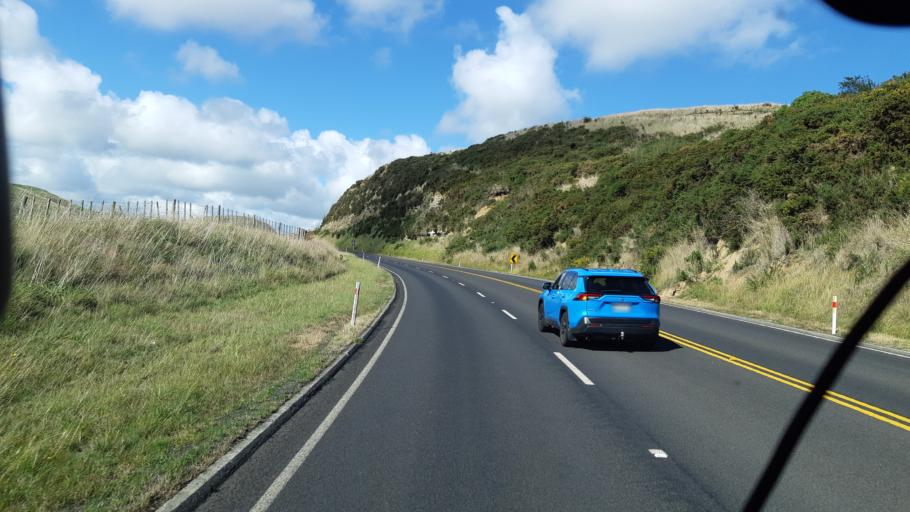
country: NZ
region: Manawatu-Wanganui
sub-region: Wanganui District
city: Wanganui
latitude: -40.0234
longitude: 175.1799
